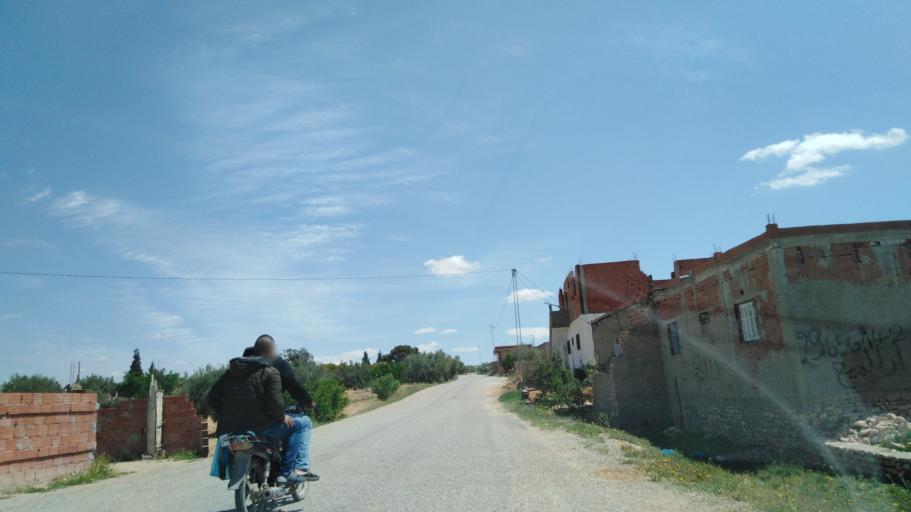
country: TN
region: Safaqis
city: Sfax
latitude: 34.7438
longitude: 10.5483
